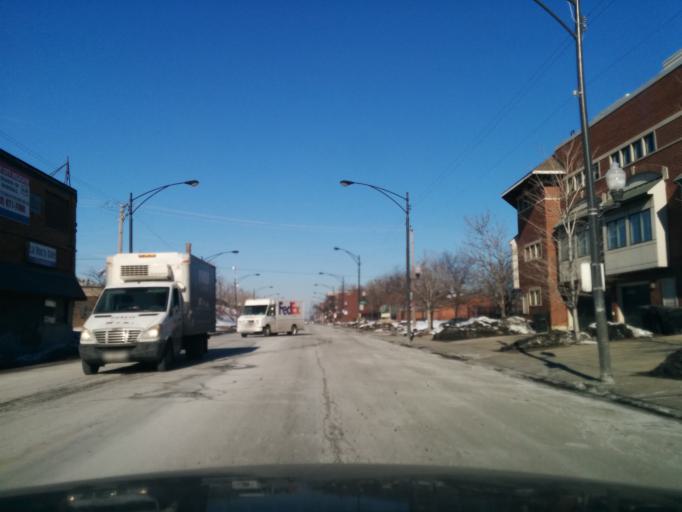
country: US
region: Illinois
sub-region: Cook County
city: Chicago
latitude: 41.8911
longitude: -87.6884
